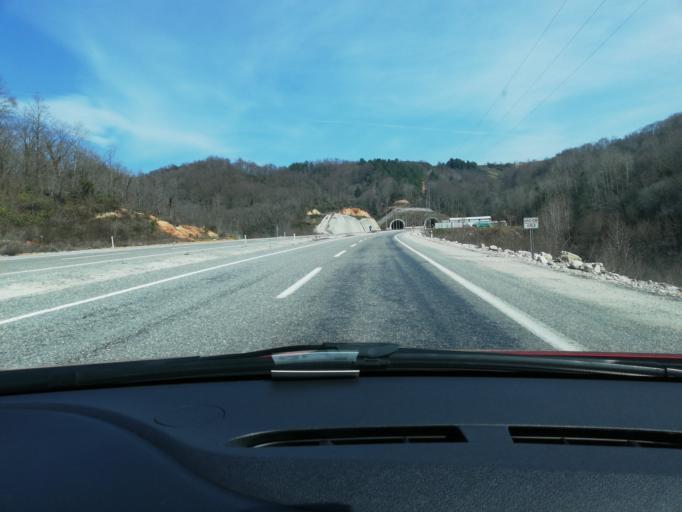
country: TR
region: Bartin
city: Amasra
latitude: 41.7738
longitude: 32.5059
